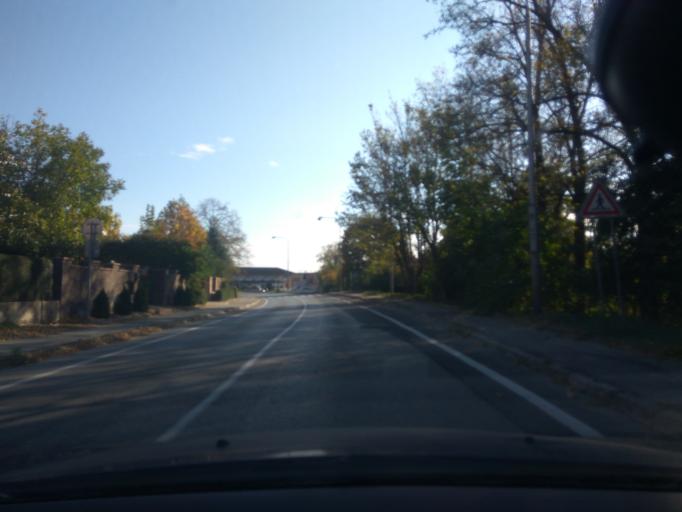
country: SK
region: Trnavsky
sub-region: Okres Trnava
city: Piestany
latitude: 48.5757
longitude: 17.8351
